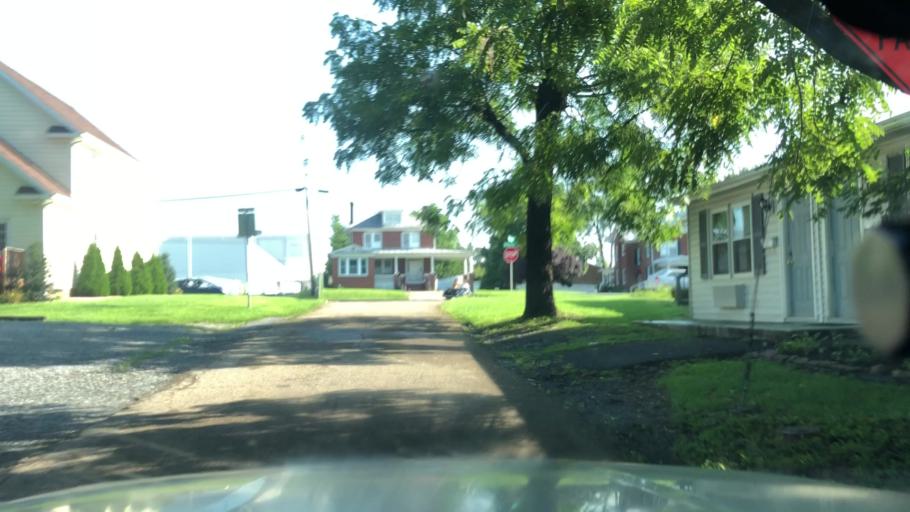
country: US
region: Virginia
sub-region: City of Harrisonburg
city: Harrisonburg
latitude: 38.4497
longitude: -78.8742
